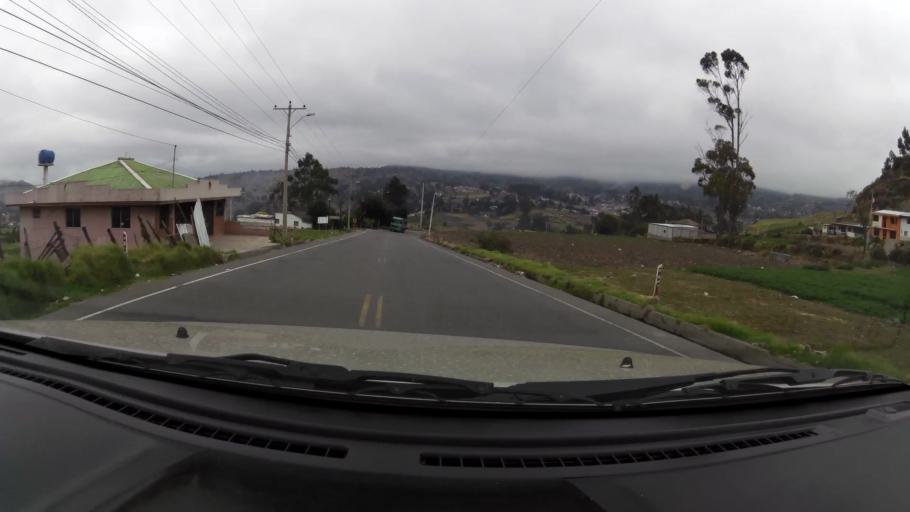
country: EC
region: Canar
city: Canar
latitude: -2.5342
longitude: -78.9323
